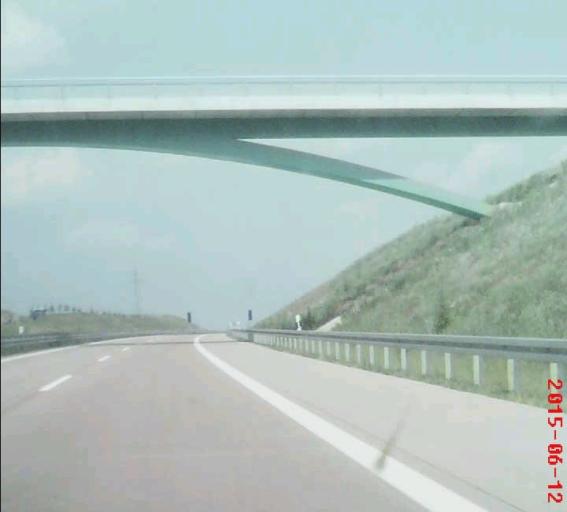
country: DE
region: Thuringia
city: Bretleben
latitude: 51.3221
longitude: 11.2421
